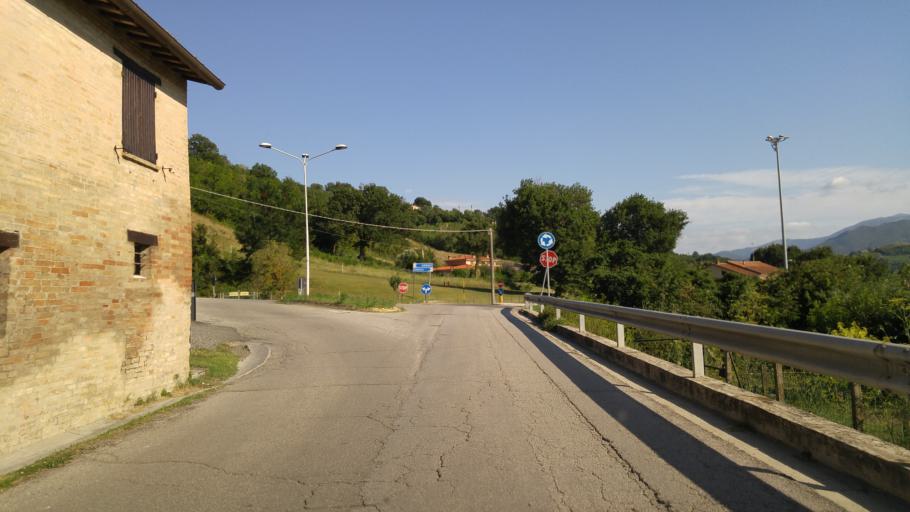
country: IT
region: The Marches
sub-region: Provincia di Pesaro e Urbino
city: Urbania
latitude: 43.6759
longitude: 12.5240
